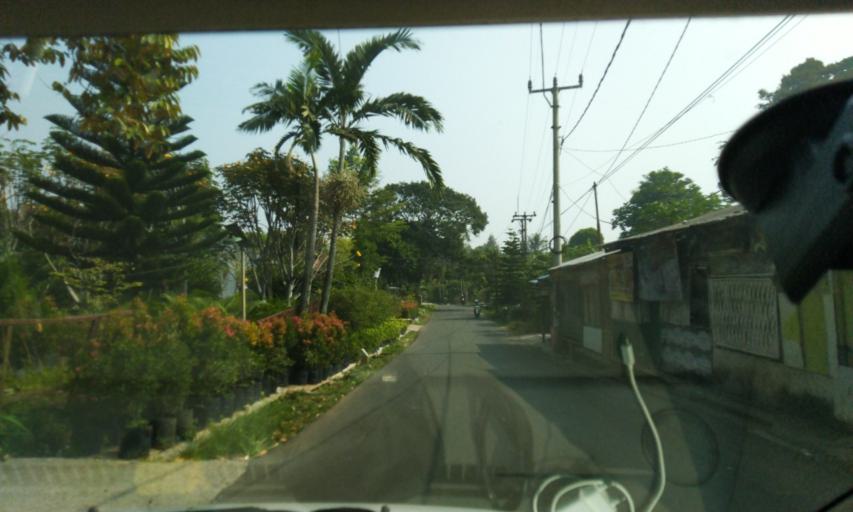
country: ID
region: West Java
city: Caringin
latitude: -6.6668
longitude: 106.8652
